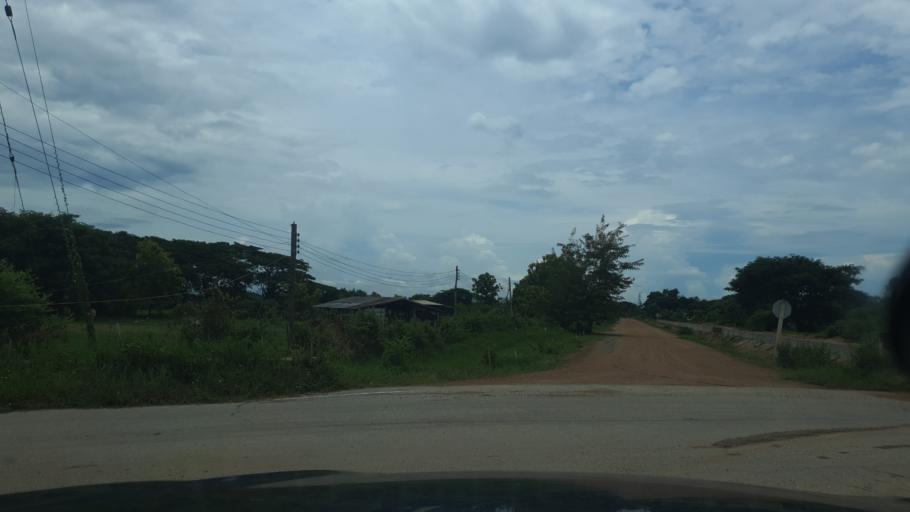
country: TH
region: Lampang
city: Hang Chat
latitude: 18.2927
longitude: 99.3719
